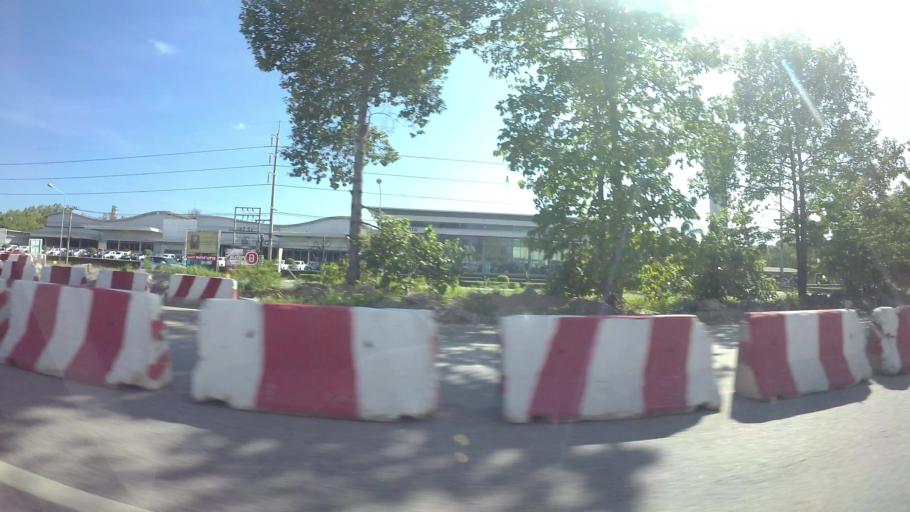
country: TH
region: Rayong
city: Rayong
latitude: 12.6668
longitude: 101.3078
